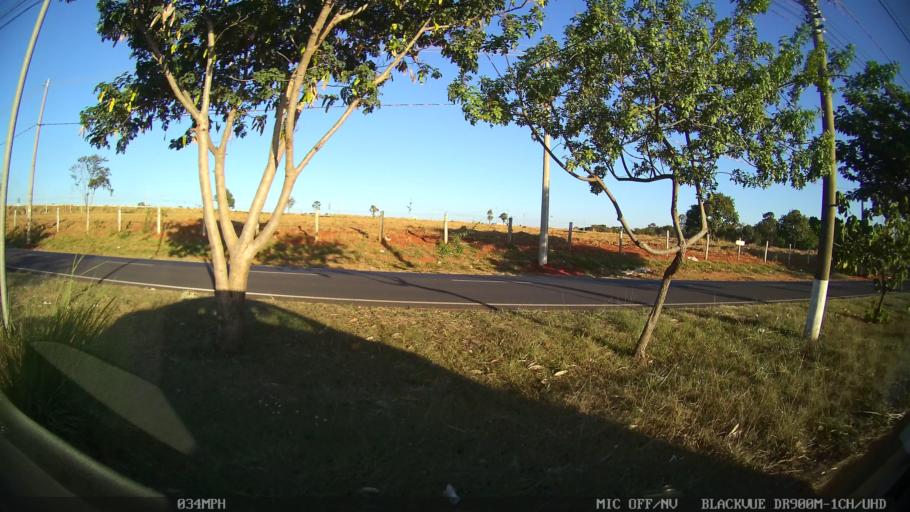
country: BR
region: Sao Paulo
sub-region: Sao Jose Do Rio Preto
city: Sao Jose do Rio Preto
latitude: -20.7637
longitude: -49.3496
